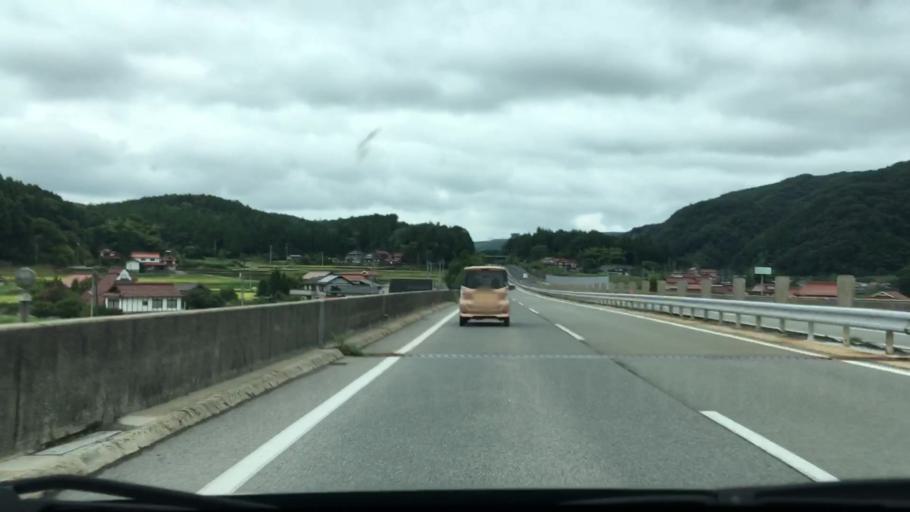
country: JP
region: Hiroshima
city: Miyoshi
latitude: 34.7715
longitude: 132.8232
